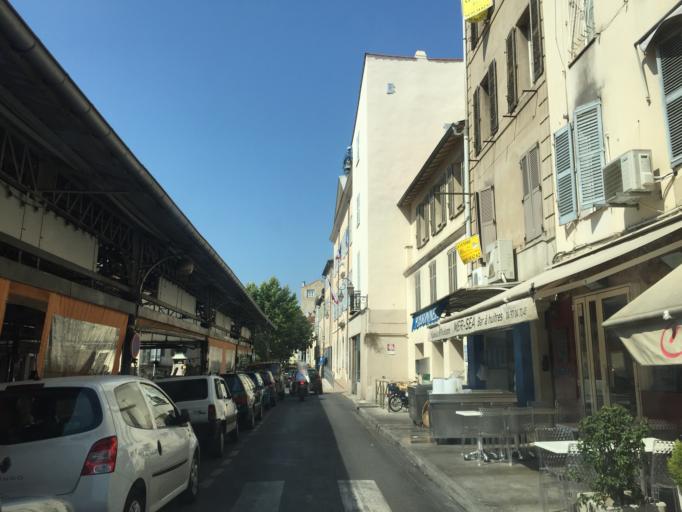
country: FR
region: Provence-Alpes-Cote d'Azur
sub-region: Departement des Alpes-Maritimes
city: Antibes
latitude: 43.5809
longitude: 7.1276
